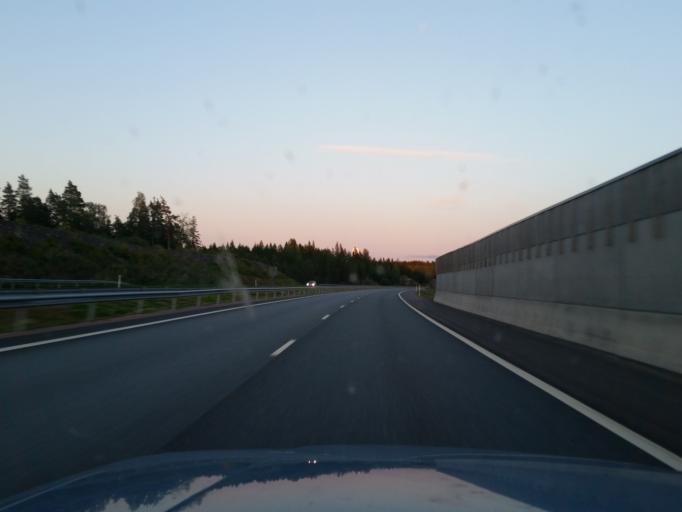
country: FI
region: Uusimaa
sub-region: Helsinki
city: Sammatti
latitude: 60.3655
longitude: 23.8757
